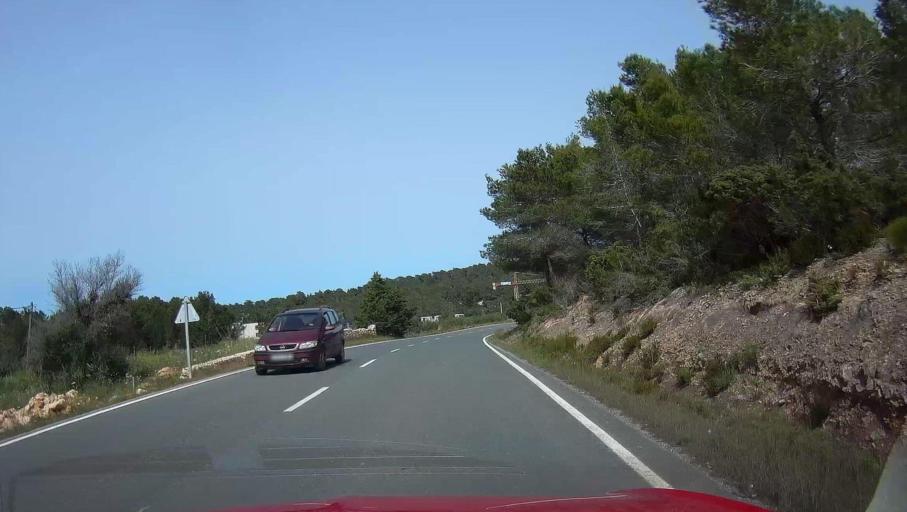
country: ES
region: Balearic Islands
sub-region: Illes Balears
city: Sant Joan de Labritja
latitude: 39.1056
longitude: 1.5173
